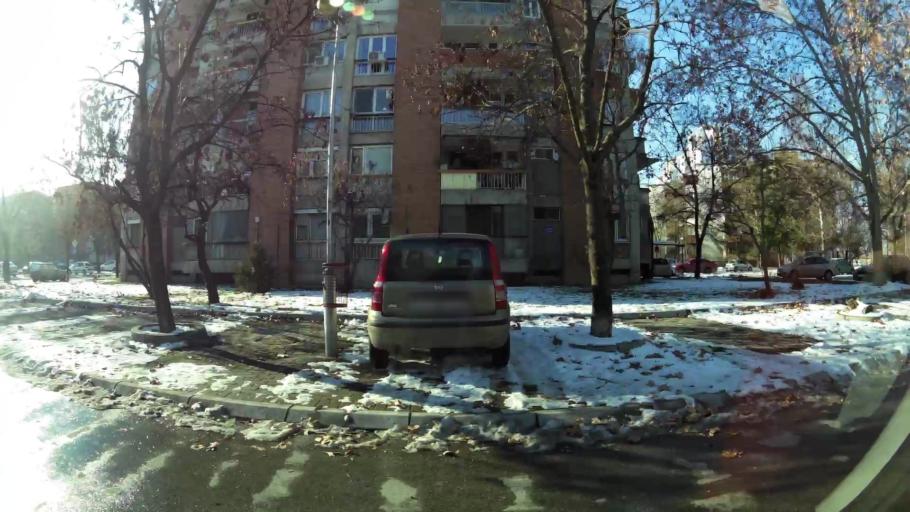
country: MK
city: Krushopek
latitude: 42.0076
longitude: 21.3875
